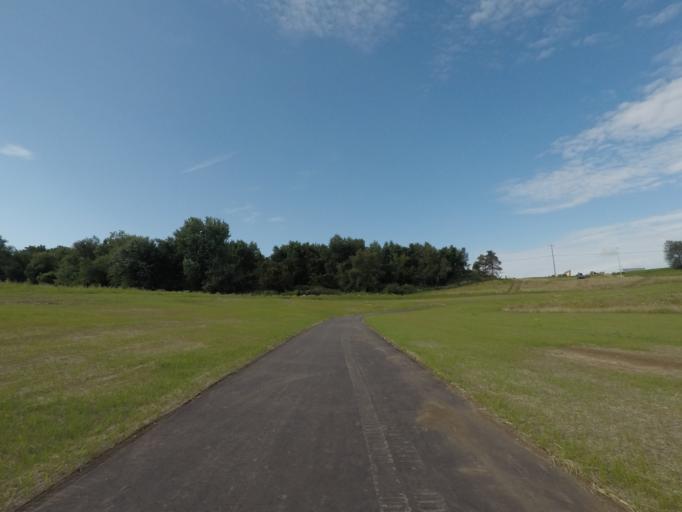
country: US
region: Wisconsin
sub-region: Dane County
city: Verona
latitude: 43.0488
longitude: -89.5509
